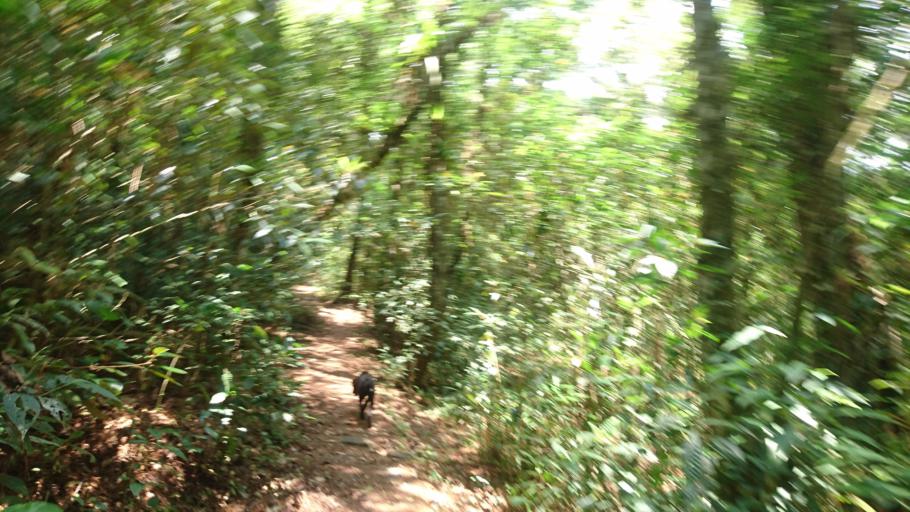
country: GT
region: Huehuetenango
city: Union
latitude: 16.1326
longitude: -91.7285
